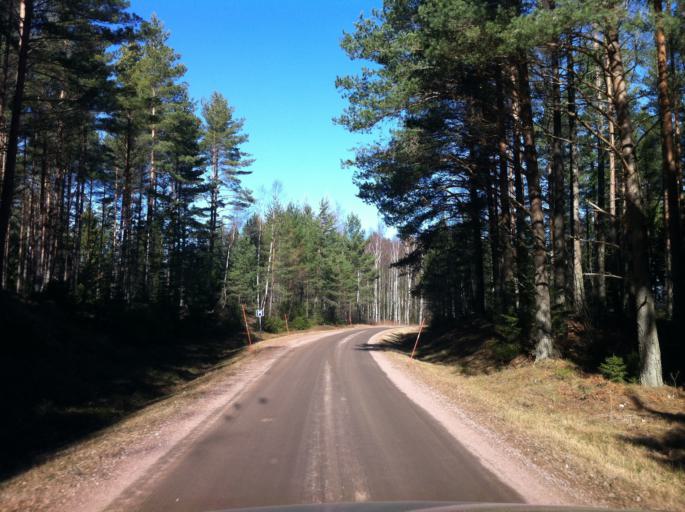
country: SE
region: Vaestra Goetaland
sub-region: Toreboda Kommun
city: Toereboda
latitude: 58.6573
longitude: 14.0890
